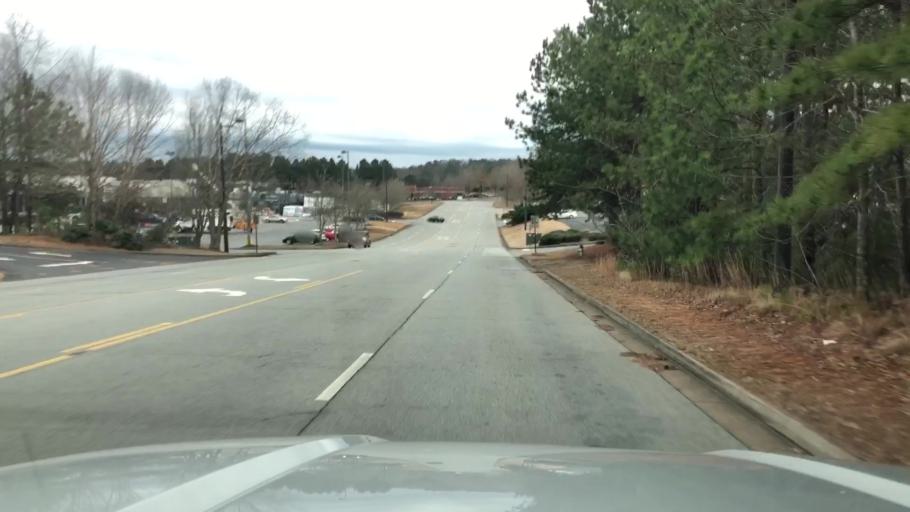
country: US
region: Georgia
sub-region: Cherokee County
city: Woodstock
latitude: 34.0835
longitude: -84.5410
